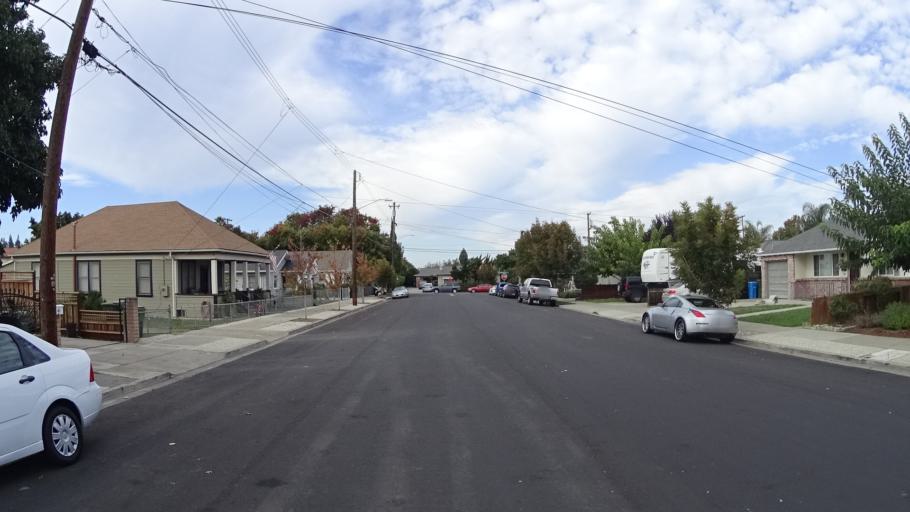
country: US
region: California
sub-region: Santa Clara County
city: Santa Clara
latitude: 37.3556
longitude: -121.9507
